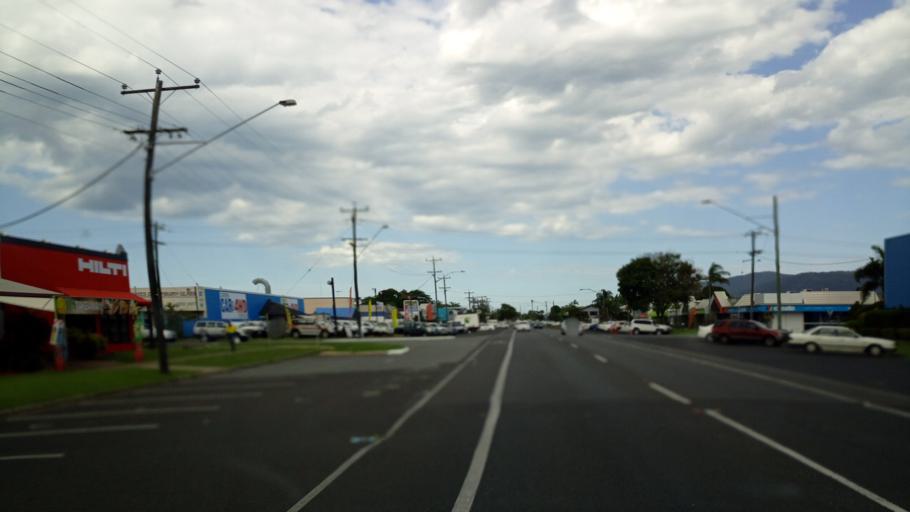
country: AU
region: Queensland
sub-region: Cairns
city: Woree
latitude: -16.9363
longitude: 145.7572
